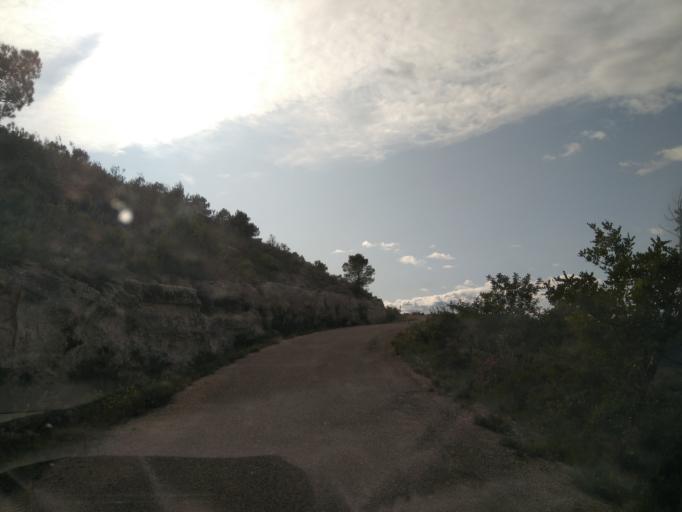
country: ES
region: Valencia
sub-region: Provincia de Valencia
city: Sumacarcer
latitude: 39.1485
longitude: -0.6472
